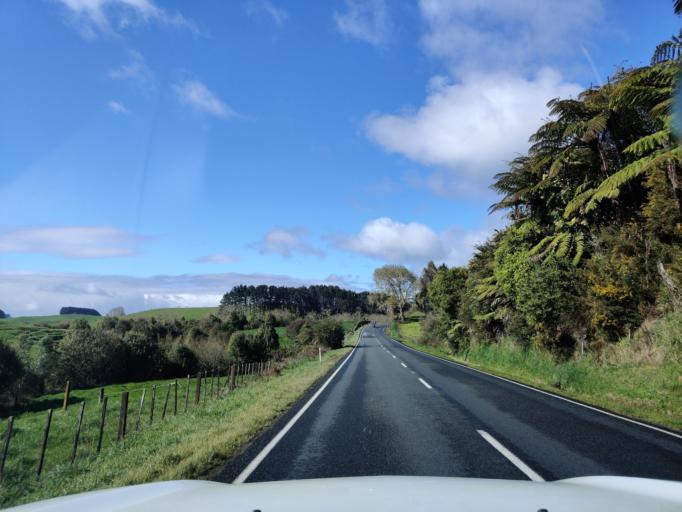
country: NZ
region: Waikato
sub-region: Otorohanga District
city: Otorohanga
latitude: -38.0776
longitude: 175.1827
